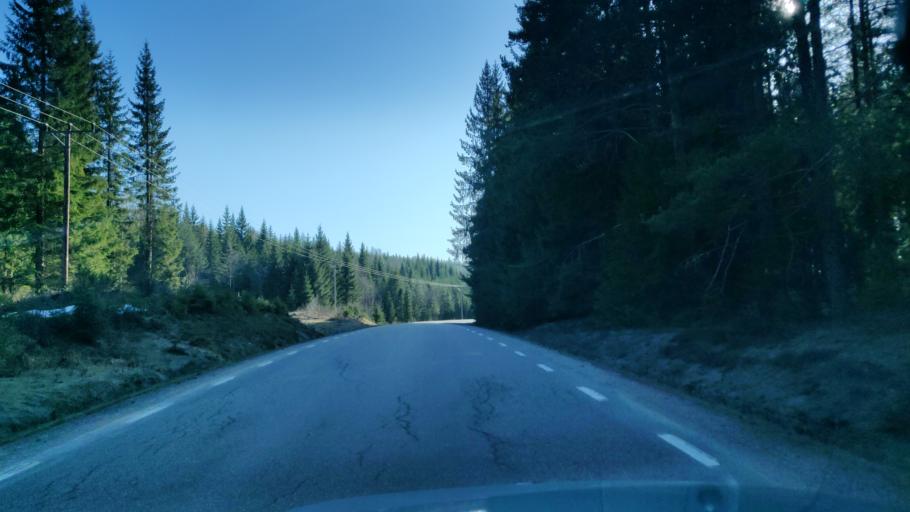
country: SE
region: Vaermland
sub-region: Munkfors Kommun
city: Munkfors
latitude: 59.9826
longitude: 13.3737
